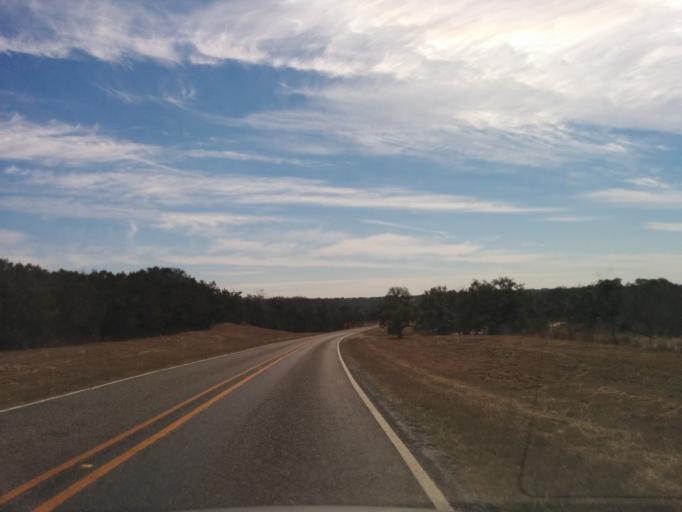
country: US
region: Texas
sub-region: Bexar County
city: Fair Oaks Ranch
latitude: 29.8998
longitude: -98.5630
